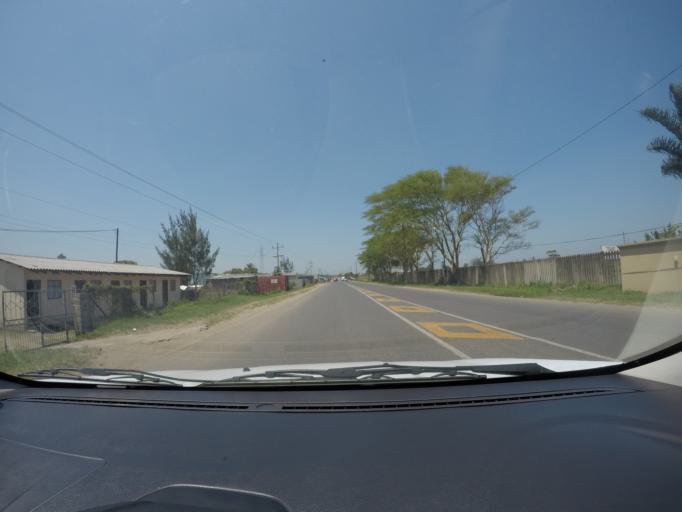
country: ZA
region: KwaZulu-Natal
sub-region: uThungulu District Municipality
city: eSikhawini
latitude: -28.8645
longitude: 31.9104
